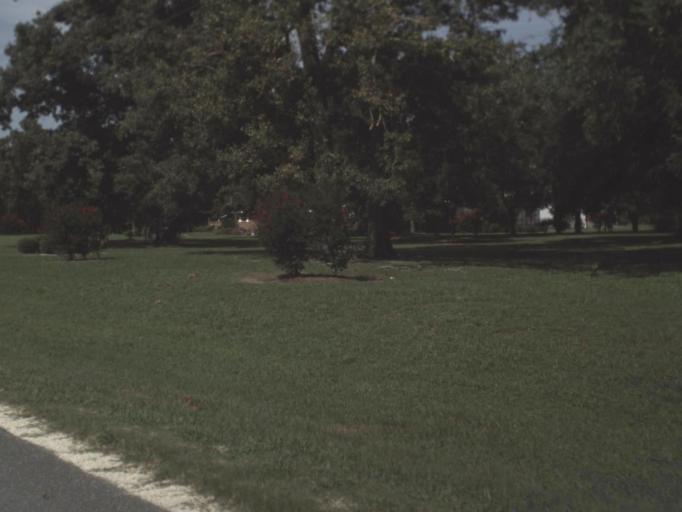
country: US
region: Florida
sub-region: Lafayette County
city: Mayo
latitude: 30.1478
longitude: -83.1640
